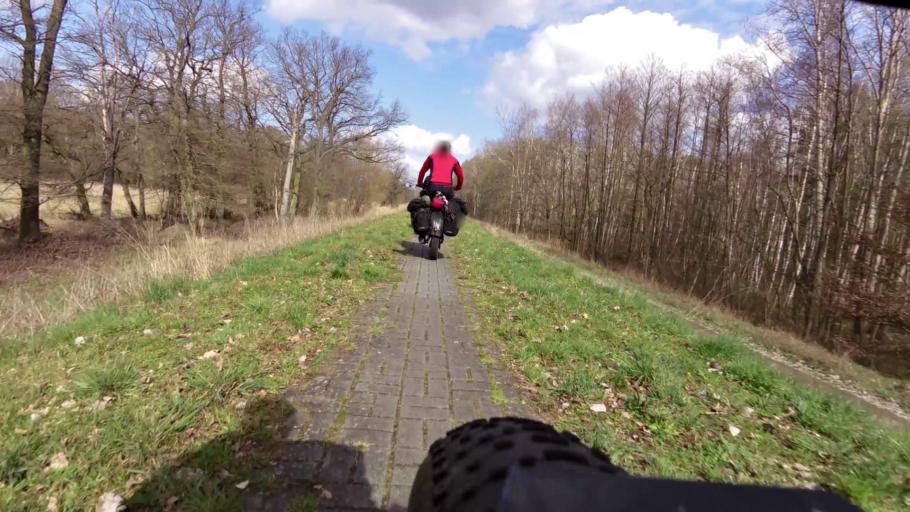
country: DE
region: Brandenburg
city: Lebus
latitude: 52.3969
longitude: 14.5412
